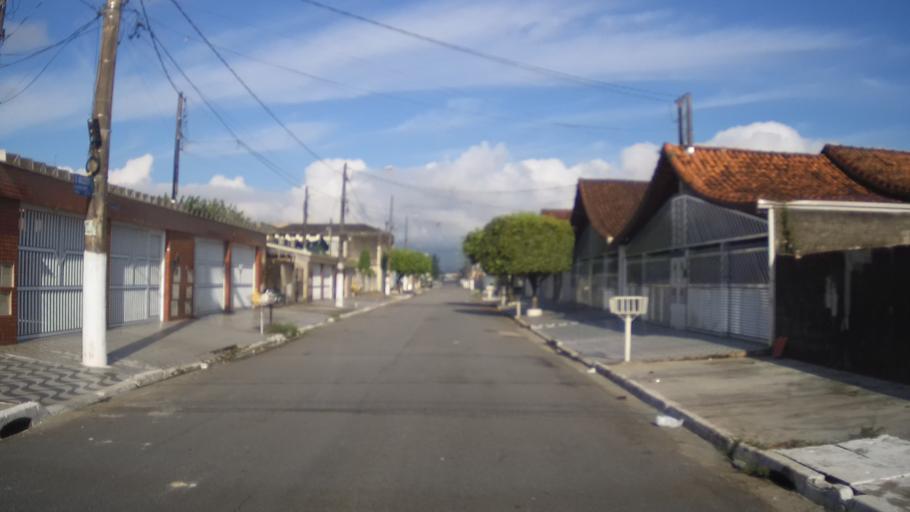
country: BR
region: Sao Paulo
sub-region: Praia Grande
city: Praia Grande
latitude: -24.0148
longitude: -46.4795
